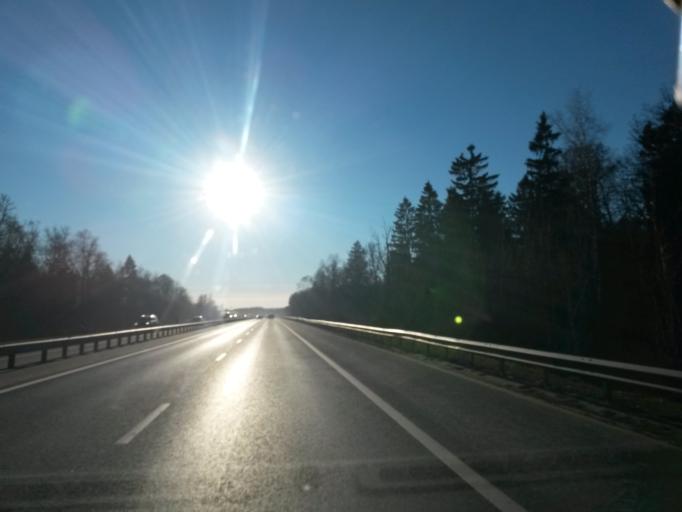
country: RU
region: Moskovskaya
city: Sofrino
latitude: 56.1151
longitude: 37.9722
